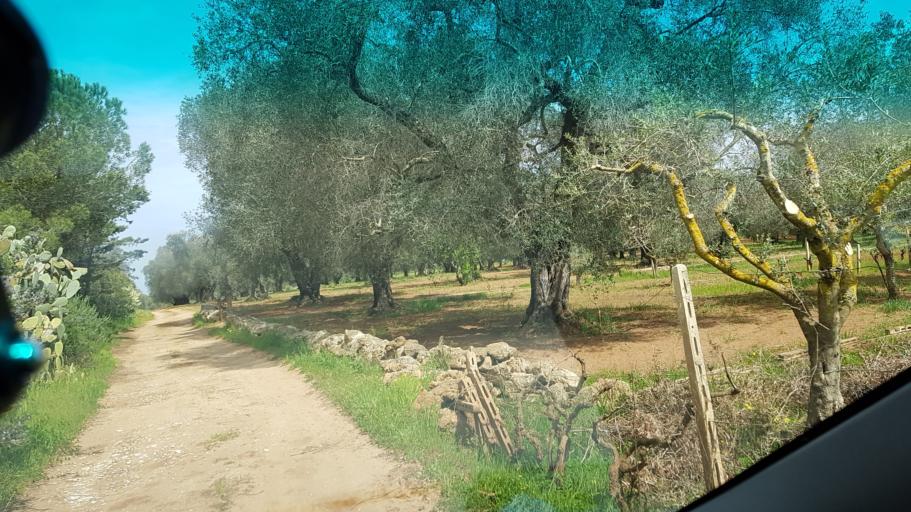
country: IT
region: Apulia
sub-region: Provincia di Brindisi
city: Mesagne
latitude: 40.6057
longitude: 17.8532
